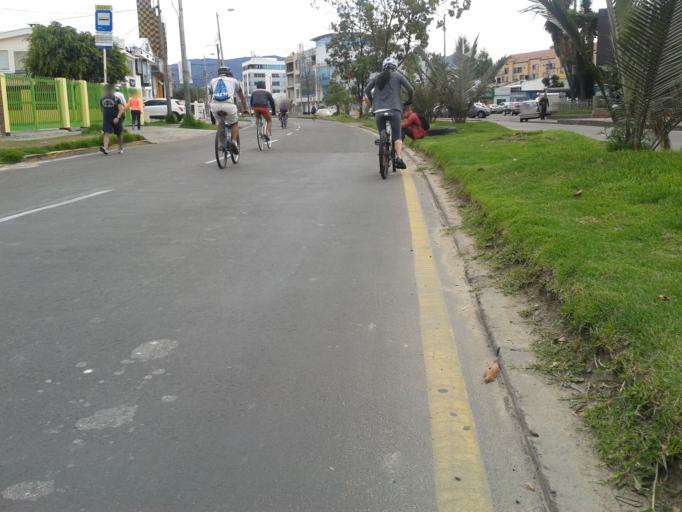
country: CO
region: Bogota D.C.
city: Barrio San Luis
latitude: 4.6988
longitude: -74.0759
